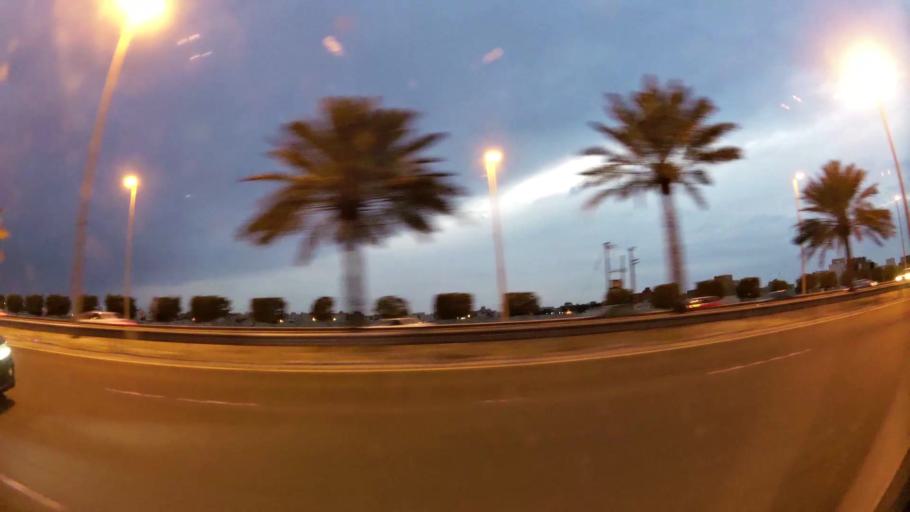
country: BH
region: Central Governorate
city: Madinat Hamad
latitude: 26.1486
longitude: 50.5091
